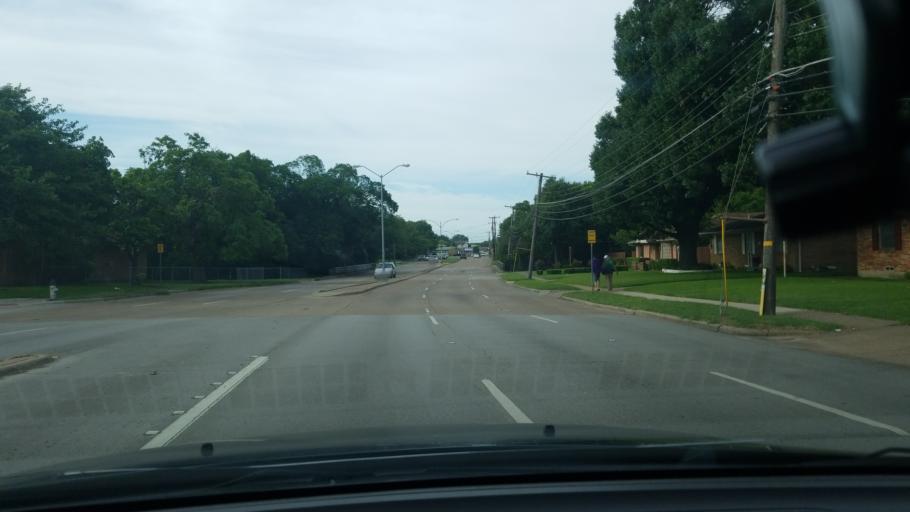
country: US
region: Texas
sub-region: Dallas County
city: Balch Springs
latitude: 32.7540
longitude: -96.6650
